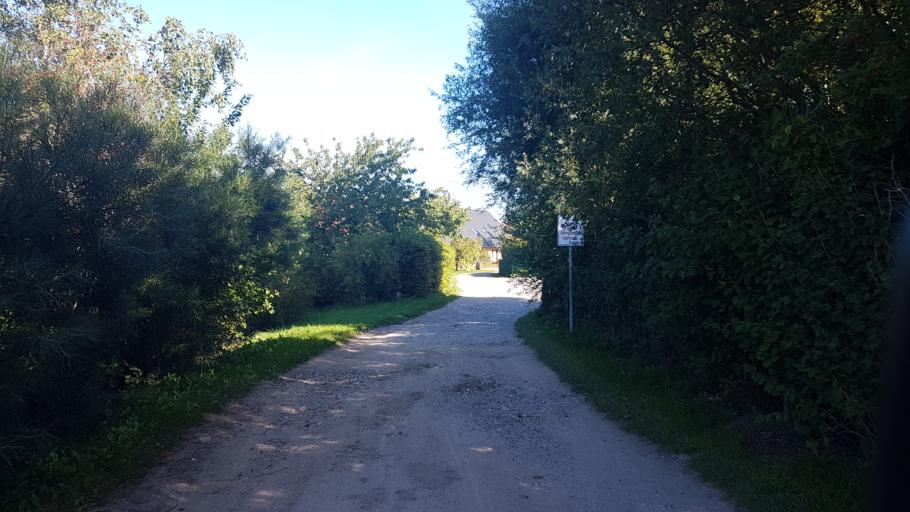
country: DE
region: Mecklenburg-Vorpommern
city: Sagard
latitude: 54.5294
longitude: 13.5164
